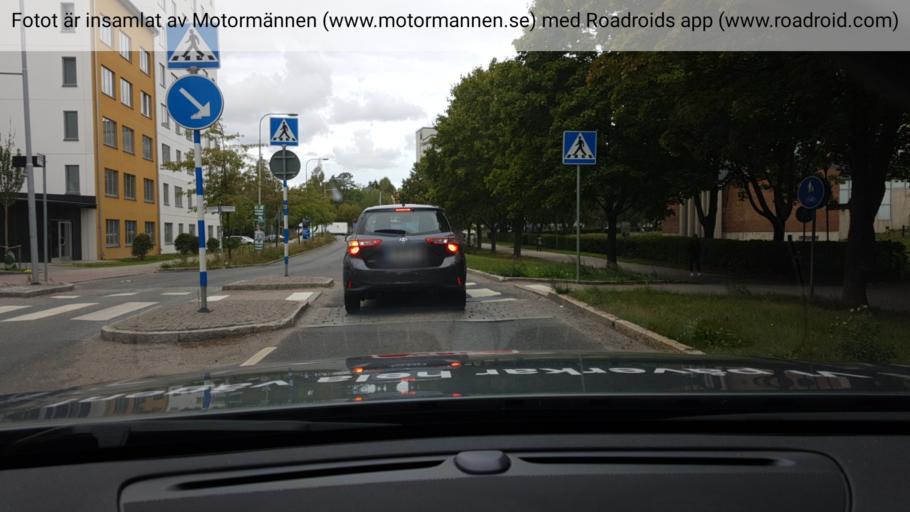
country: SE
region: Stockholm
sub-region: Huddinge Kommun
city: Huddinge
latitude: 59.2423
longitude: 17.9950
